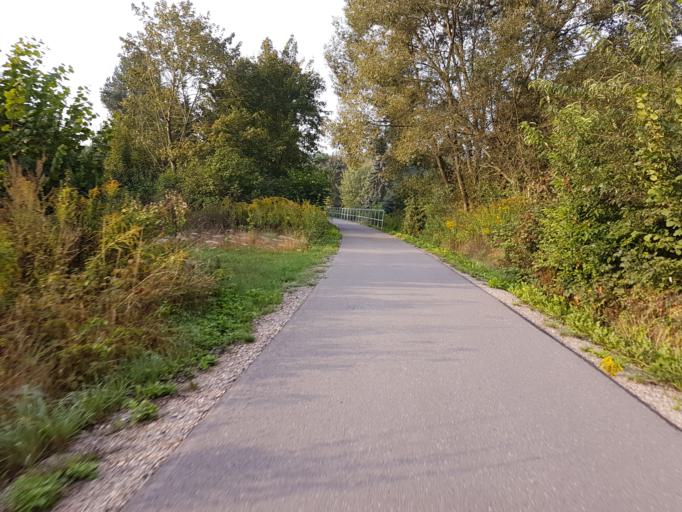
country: DE
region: Saxony
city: Wittgensdorf
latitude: 50.8949
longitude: 12.8920
